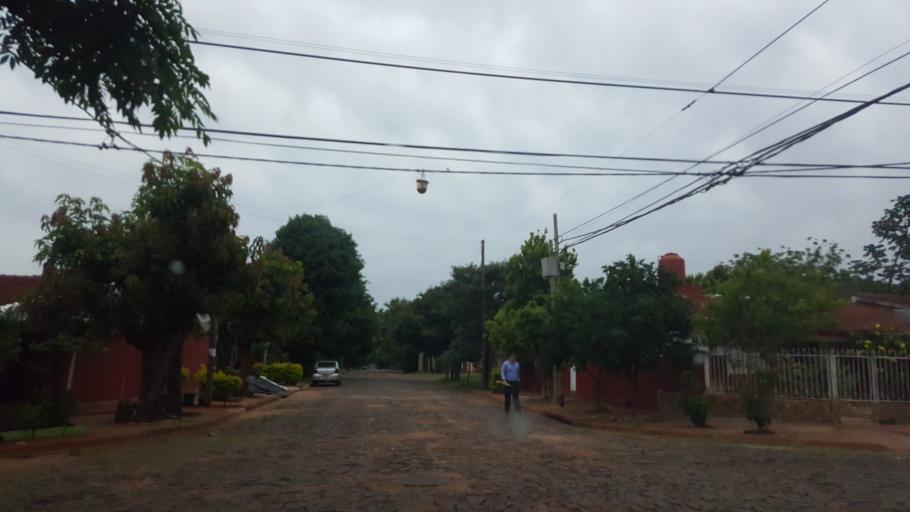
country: AR
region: Misiones
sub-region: Departamento de Capital
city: Posadas
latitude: -27.3726
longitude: -55.9230
